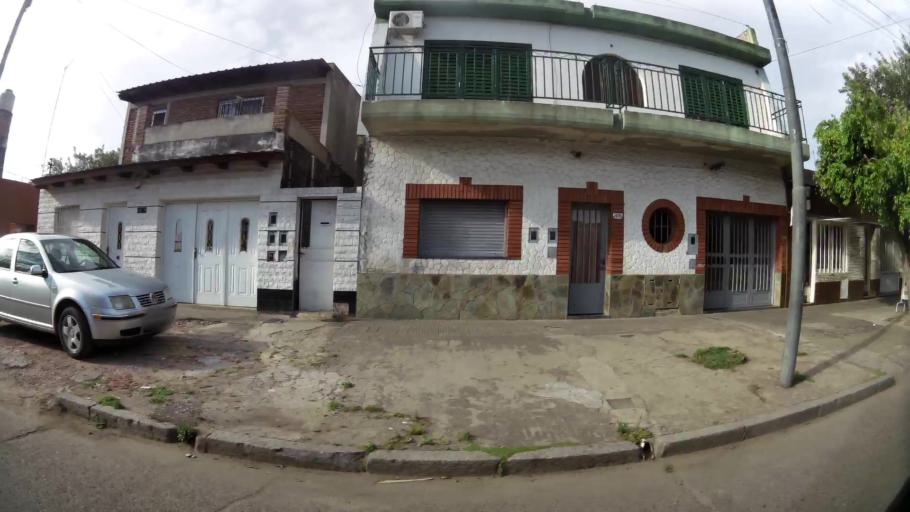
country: AR
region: Santa Fe
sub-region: Departamento de Rosario
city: Rosario
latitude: -32.9754
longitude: -60.6802
